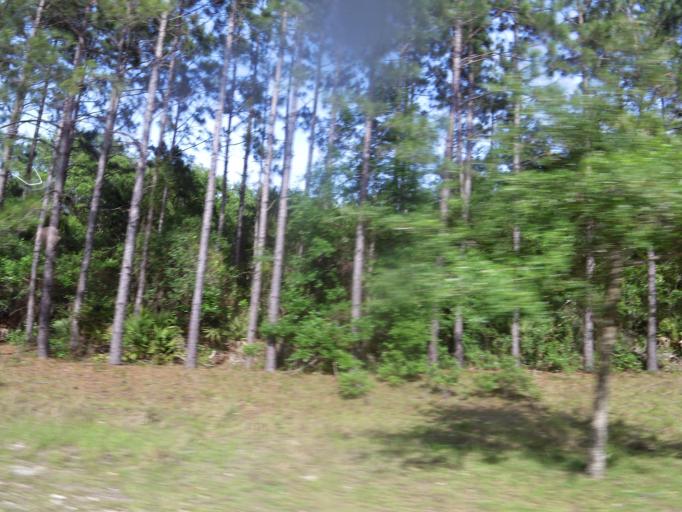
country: US
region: Florida
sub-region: Nassau County
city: Fernandina Beach
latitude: 30.4941
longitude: -81.4910
